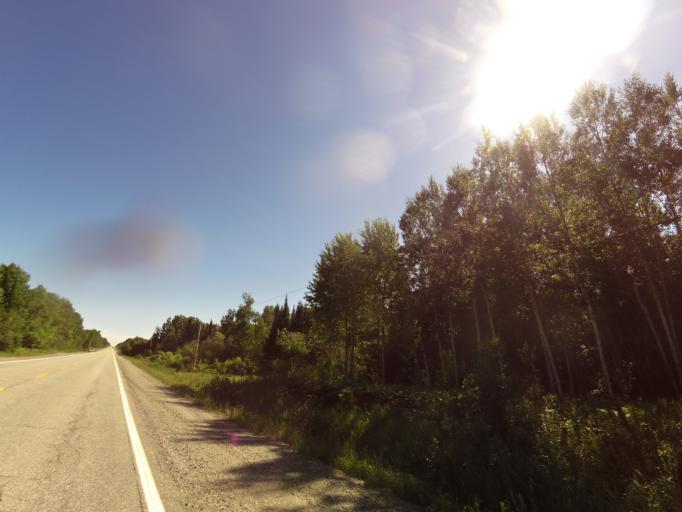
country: CA
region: Quebec
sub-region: Abitibi-Temiscamingue
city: Senneterre
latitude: 48.1792
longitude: -77.3619
